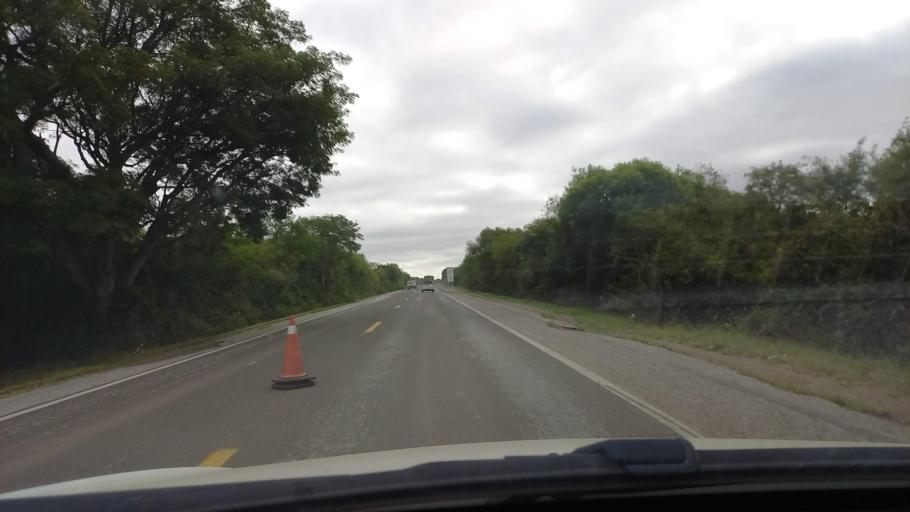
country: BR
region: Rio Grande do Sul
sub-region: Dom Pedrito
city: Dom Pedrito
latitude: -30.9565
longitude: -54.6896
